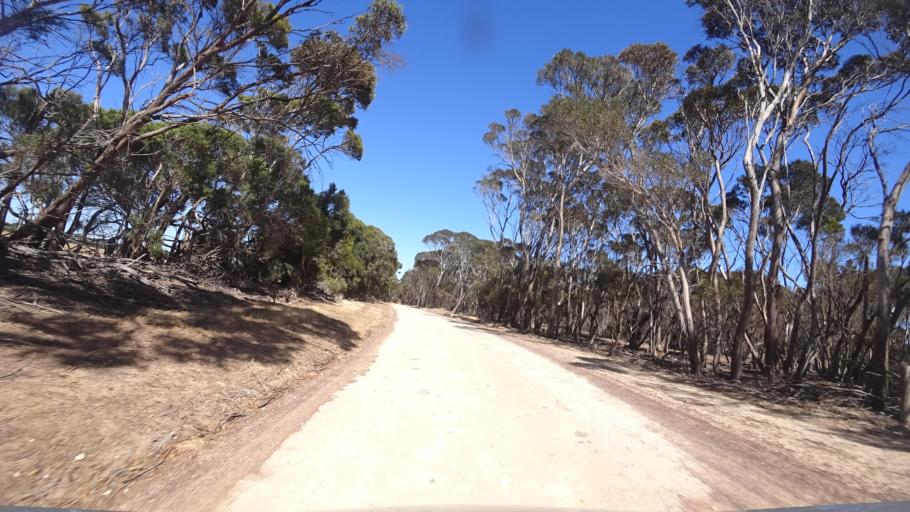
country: AU
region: South Australia
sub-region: Kangaroo Island
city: Kingscote
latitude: -35.7497
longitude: 137.7307
